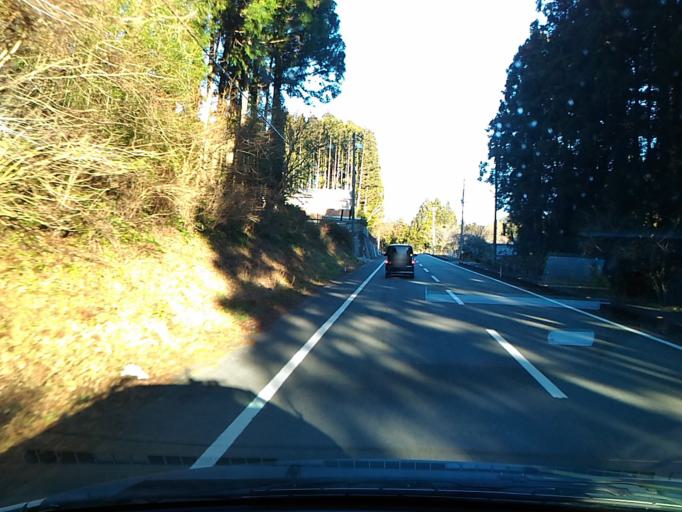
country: JP
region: Ibaraki
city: Kitaibaraki
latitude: 36.9280
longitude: 140.6943
